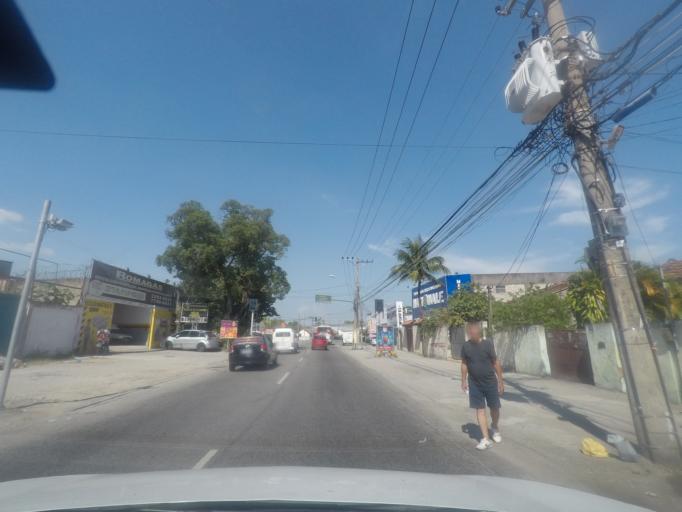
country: BR
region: Rio de Janeiro
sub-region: Nilopolis
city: Nilopolis
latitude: -22.8777
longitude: -43.4469
